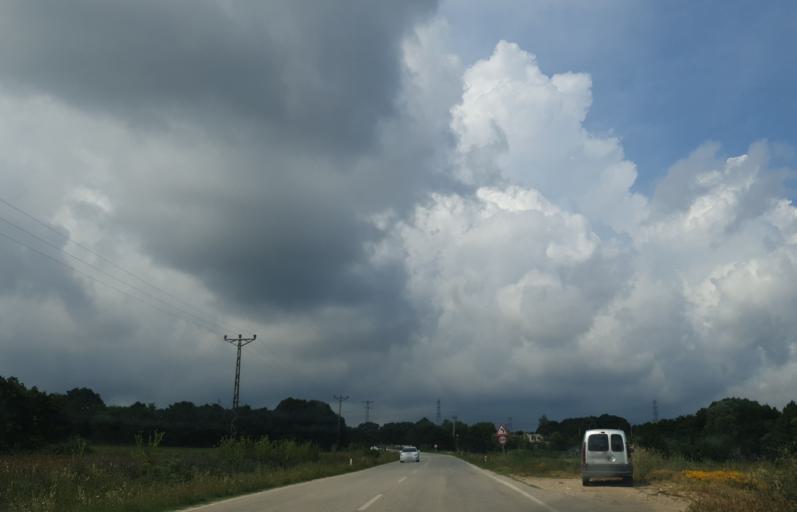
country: TR
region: Tekirdag
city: Saray
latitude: 41.4741
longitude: 27.9550
